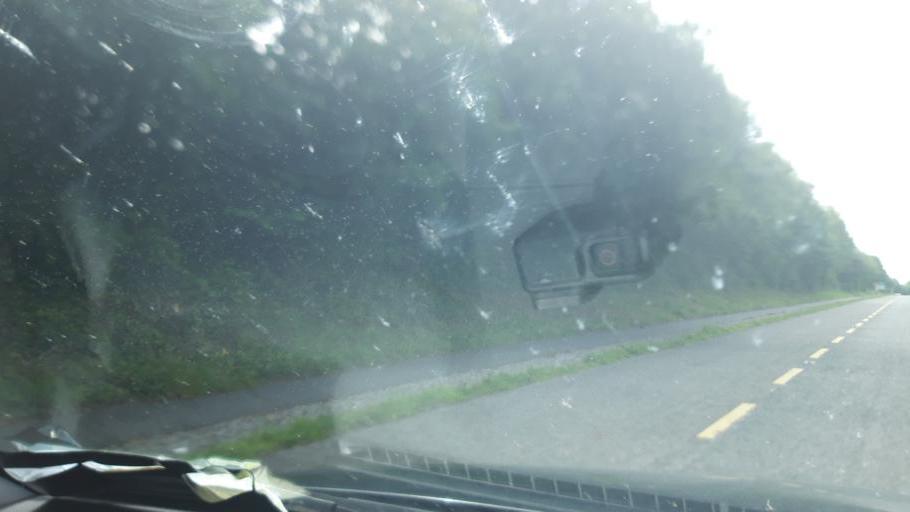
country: IE
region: Leinster
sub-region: Kilkenny
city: Callan
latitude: 52.5428
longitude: -7.3968
